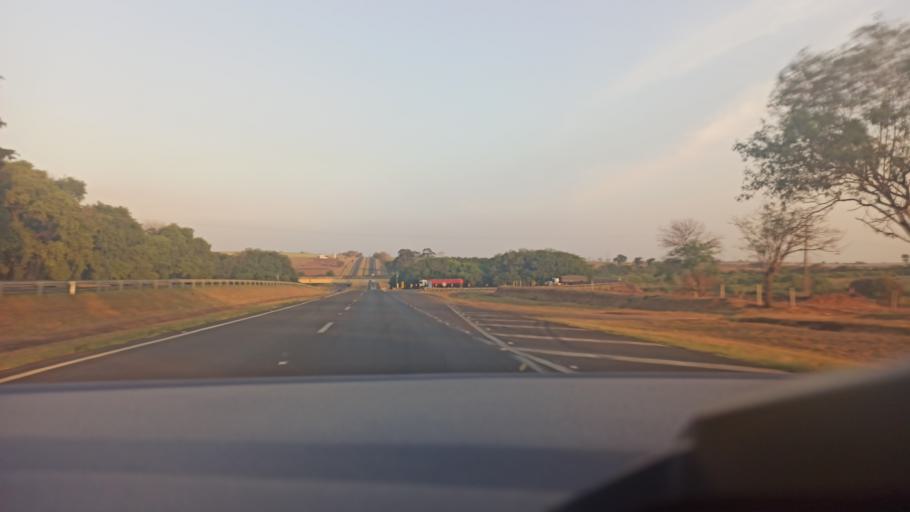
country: BR
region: Sao Paulo
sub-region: Santa Adelia
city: Santa Adelia
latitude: -21.3695
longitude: -48.7518
